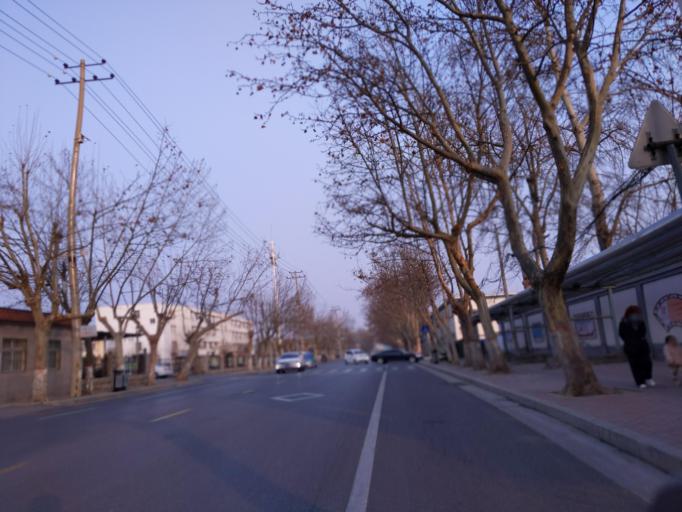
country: CN
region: Henan Sheng
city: Zhongyuanlu
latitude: 35.7862
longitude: 115.0633
